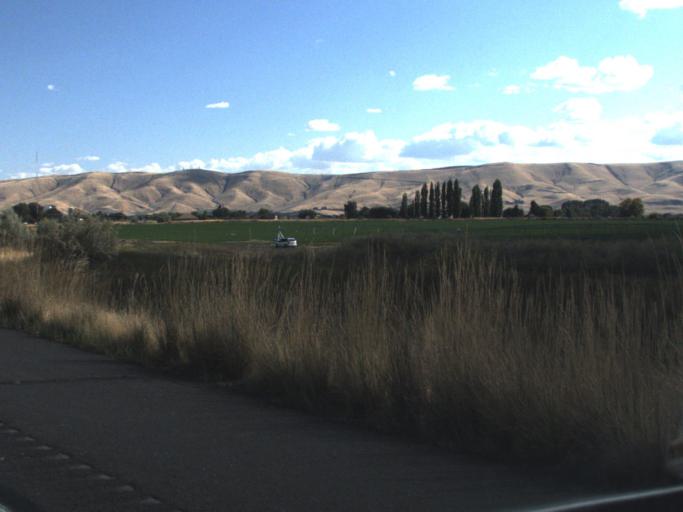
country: US
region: Washington
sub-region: Benton County
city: Prosser
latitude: 46.2392
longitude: -119.8231
